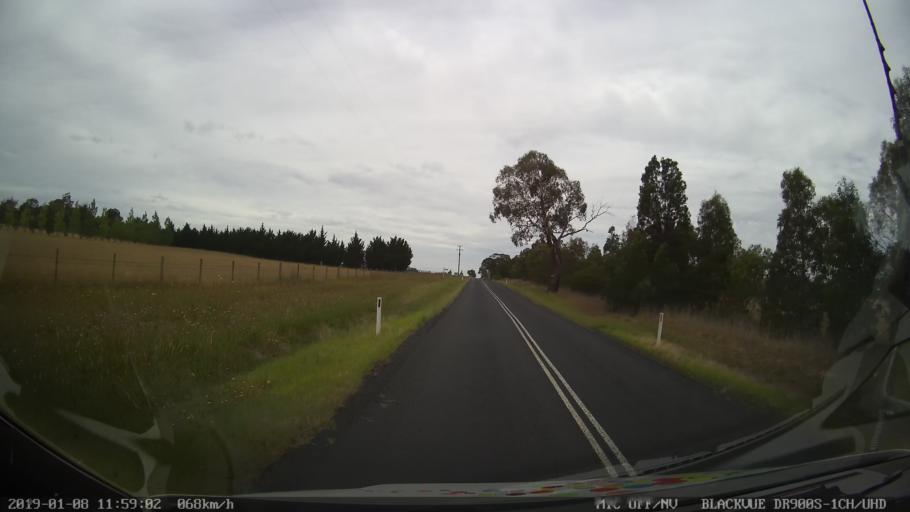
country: AU
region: New South Wales
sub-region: Armidale Dumaresq
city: Armidale
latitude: -30.4578
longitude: 151.5822
